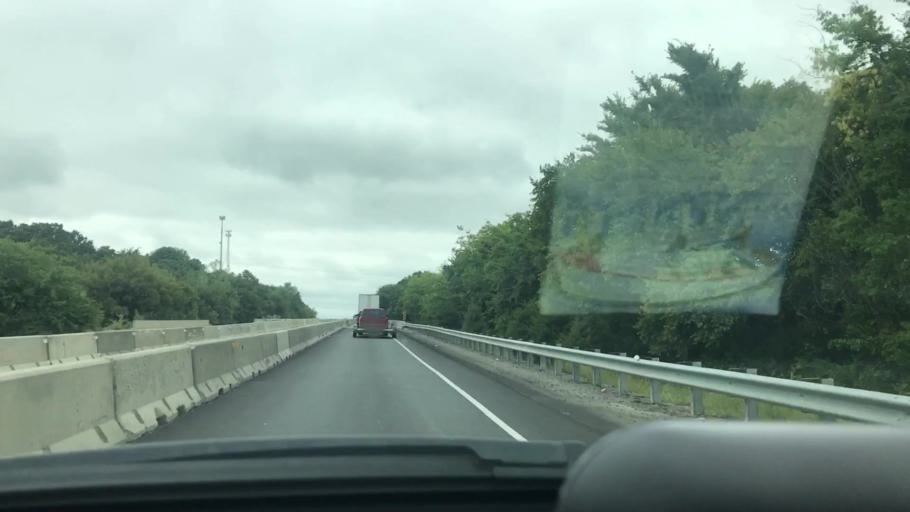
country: US
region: Oklahoma
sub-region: McIntosh County
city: Eufaula
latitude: 35.2838
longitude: -95.5931
